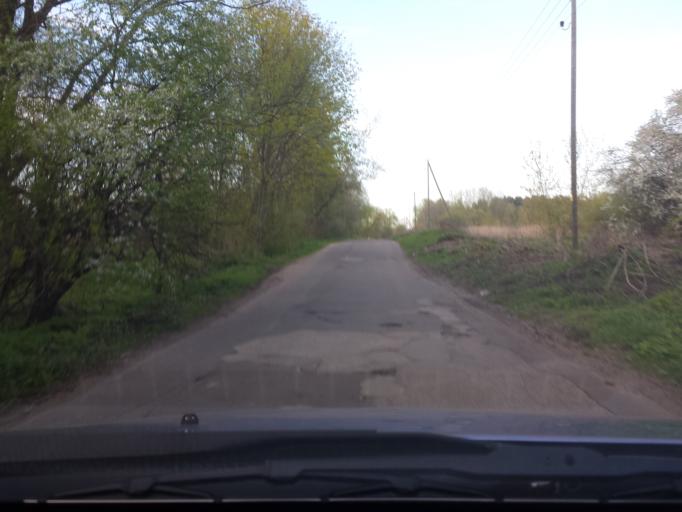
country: LV
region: Riga
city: Jaunciems
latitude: 56.9934
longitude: 24.2149
